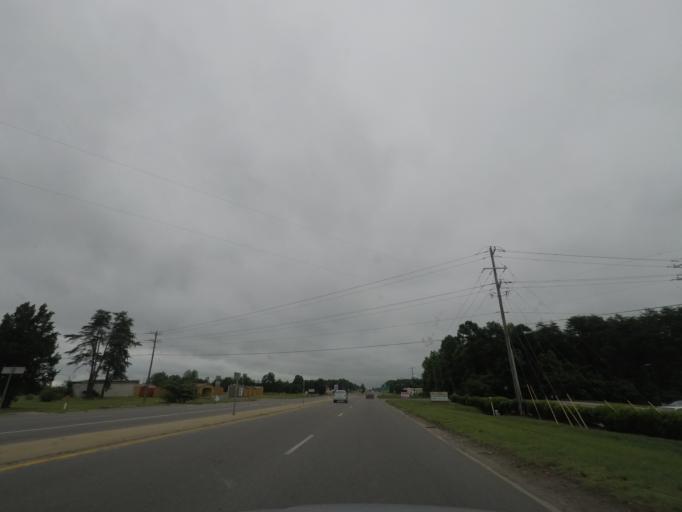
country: US
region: Virginia
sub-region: Fluvanna County
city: Palmyra
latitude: 37.9710
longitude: -78.2191
